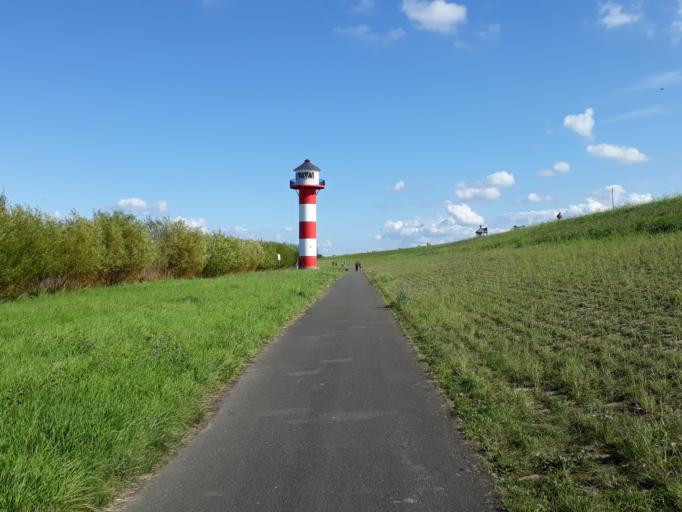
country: DE
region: Lower Saxony
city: Grunendeich
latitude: 53.5700
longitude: 9.6382
